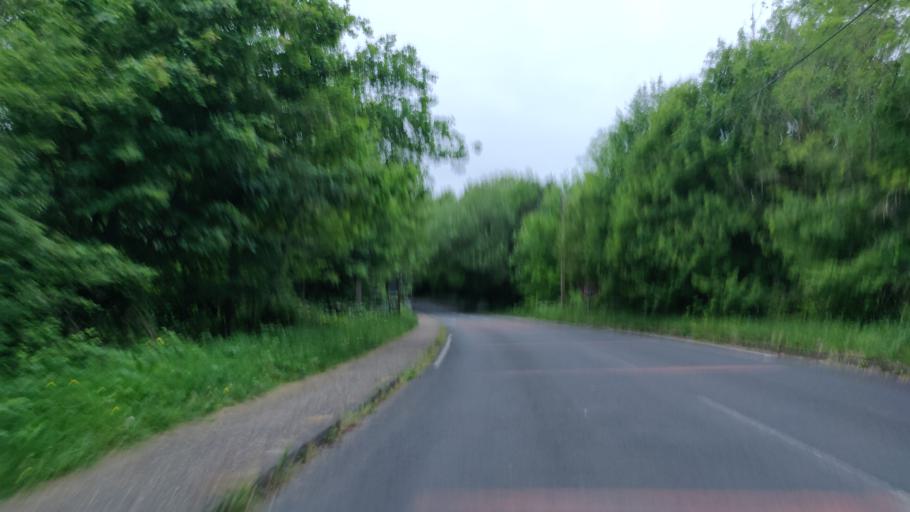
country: GB
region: England
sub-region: West Sussex
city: Southwater
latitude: 51.0360
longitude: -0.3429
